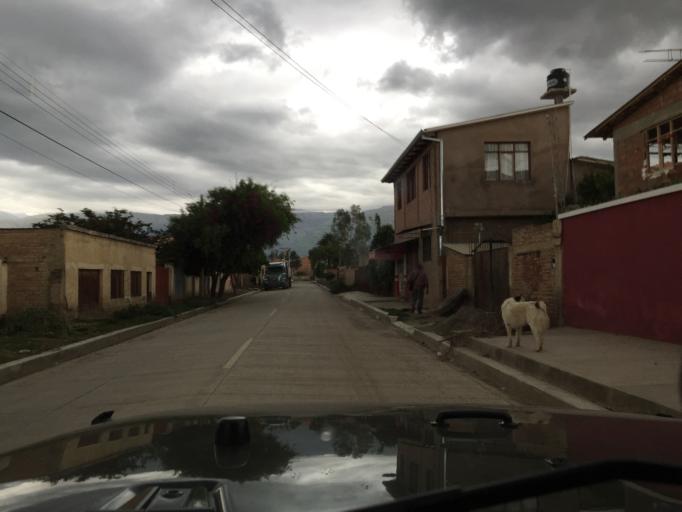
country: BO
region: Cochabamba
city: Cochabamba
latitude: -17.3996
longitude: -66.2126
